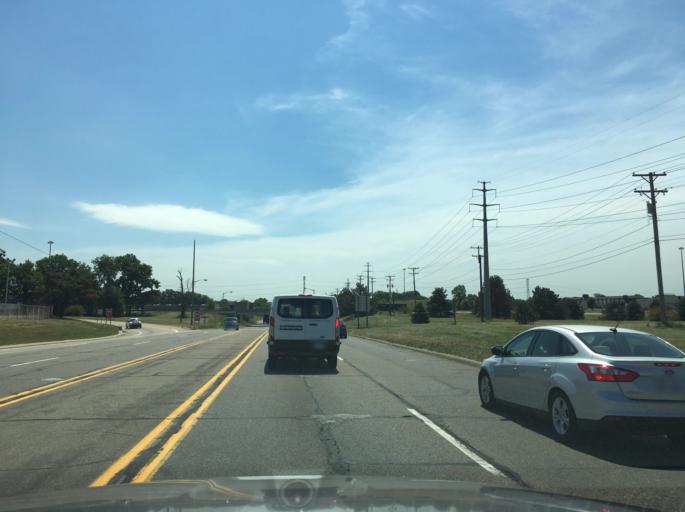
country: US
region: Michigan
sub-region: Wayne County
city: Melvindale
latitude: 42.2864
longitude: -83.1992
